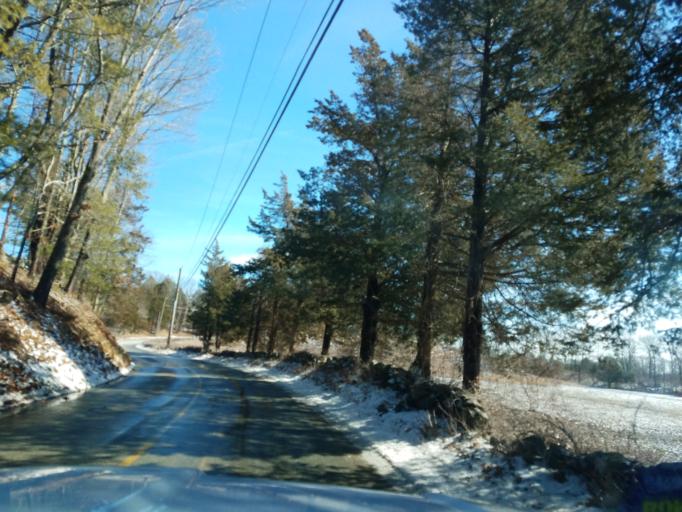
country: US
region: Connecticut
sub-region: New London County
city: Preston City
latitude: 41.4996
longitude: -71.9086
